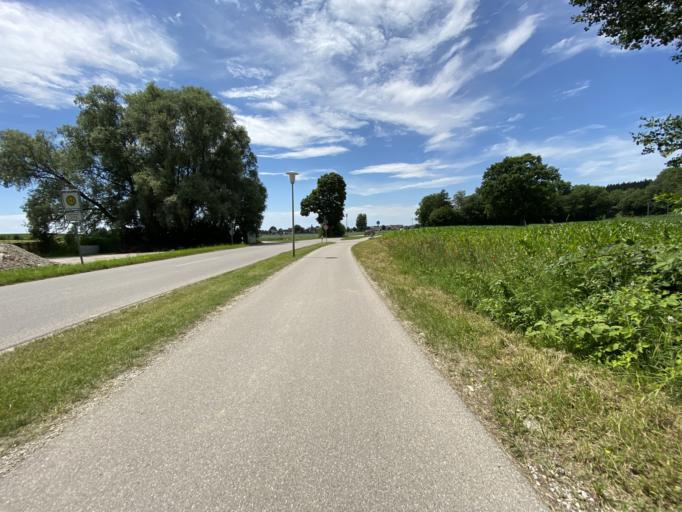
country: DE
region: Bavaria
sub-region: Upper Bavaria
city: Gilching
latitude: 48.1078
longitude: 11.3146
